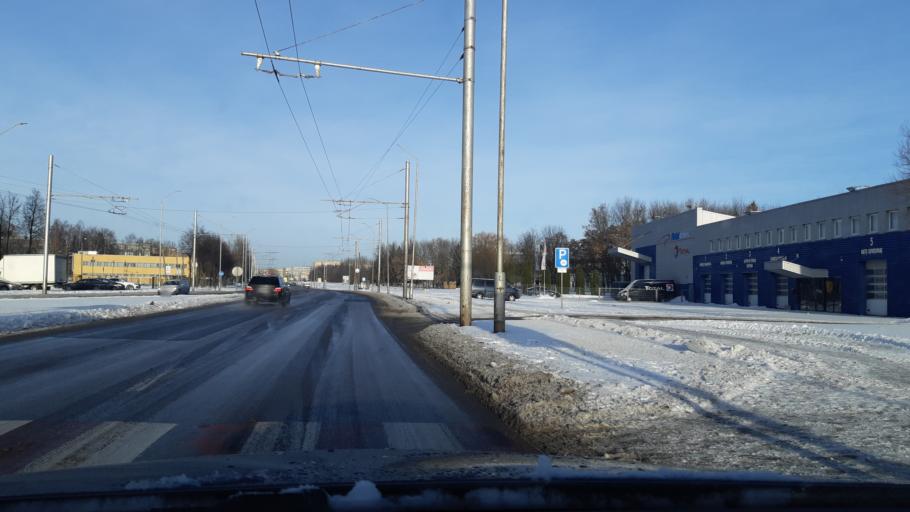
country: LT
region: Kauno apskritis
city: Dainava (Kaunas)
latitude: 54.9180
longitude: 23.9845
